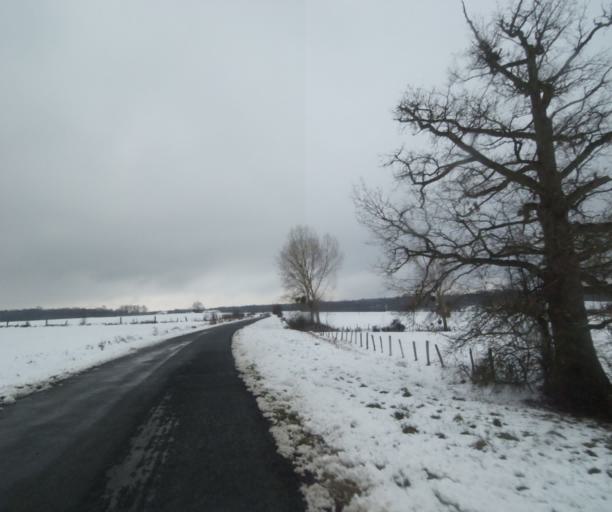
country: FR
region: Champagne-Ardenne
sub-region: Departement de la Haute-Marne
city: Laneuville-a-Remy
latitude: 48.4794
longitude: 4.8781
